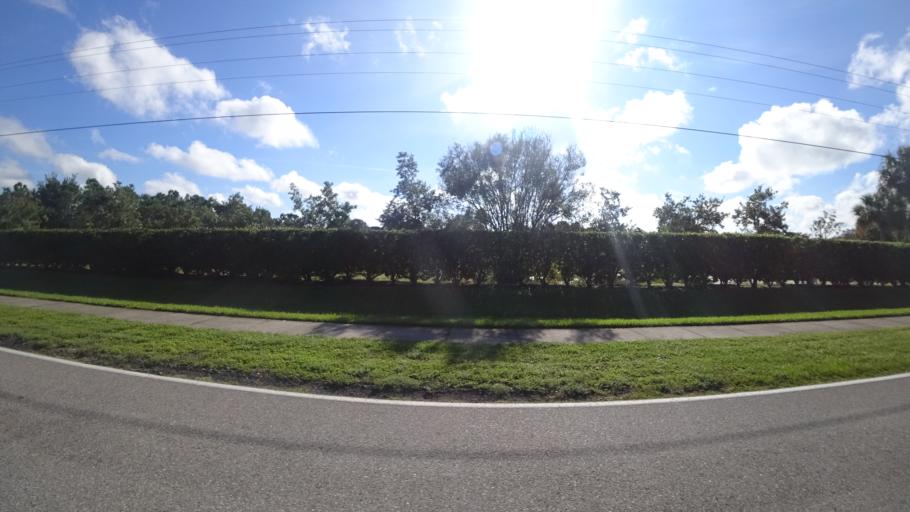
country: US
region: Florida
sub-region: Manatee County
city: Ellenton
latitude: 27.5882
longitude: -82.5117
